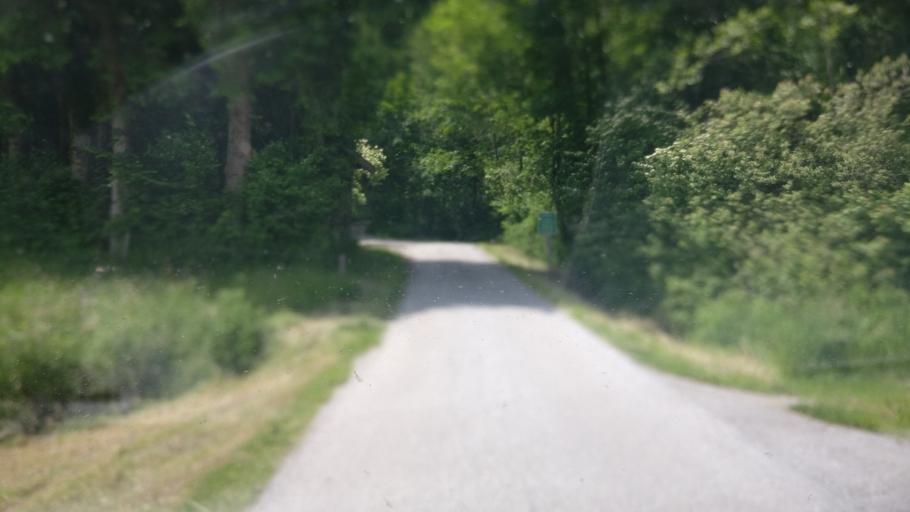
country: AT
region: Salzburg
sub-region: Politischer Bezirk Hallein
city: Kuchl
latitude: 47.6409
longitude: 13.1244
